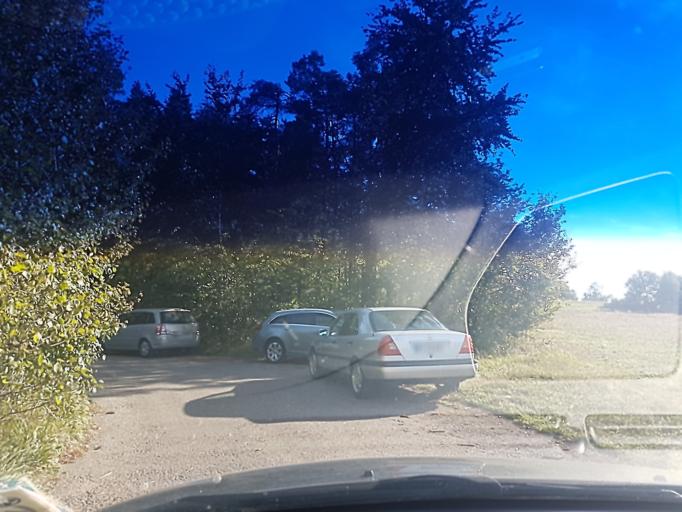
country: DE
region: Bavaria
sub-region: Upper Franconia
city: Schesslitz
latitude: 50.0176
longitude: 11.0352
